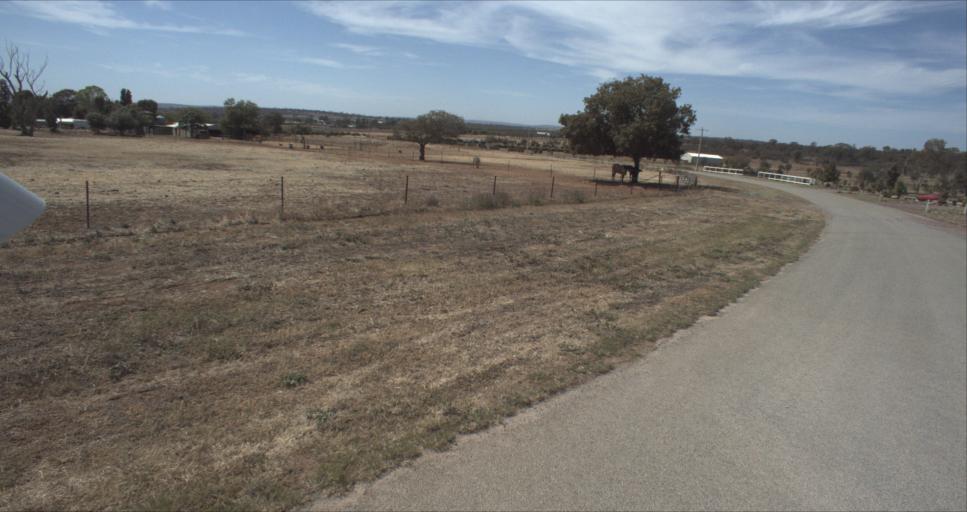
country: AU
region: New South Wales
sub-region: Leeton
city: Leeton
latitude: -34.5763
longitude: 146.4514
